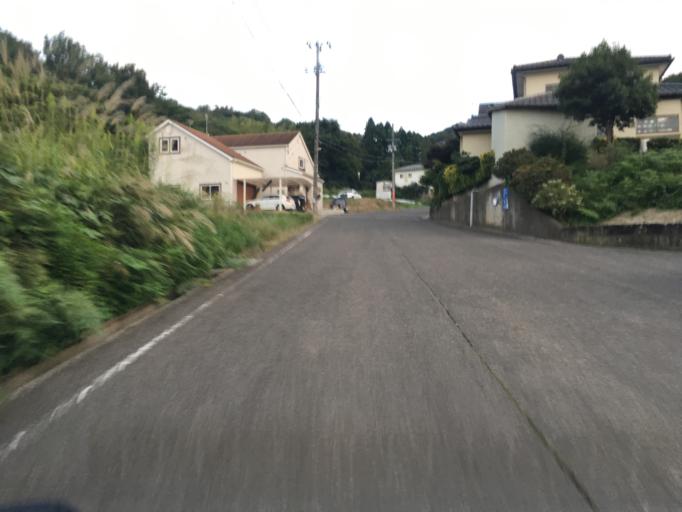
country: JP
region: Fukushima
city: Fukushima-shi
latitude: 37.7376
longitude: 140.4884
